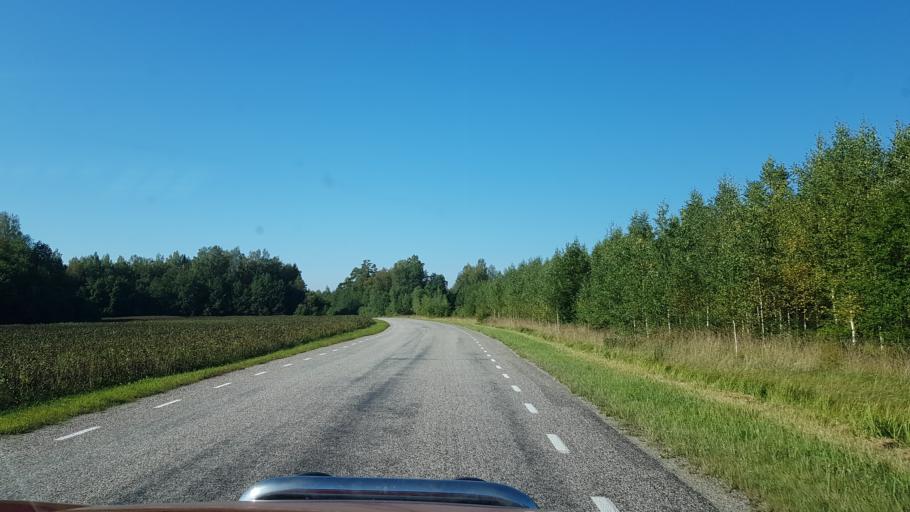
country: EE
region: Jogevamaa
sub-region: Jogeva linn
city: Jogeva
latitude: 58.6517
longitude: 26.3516
